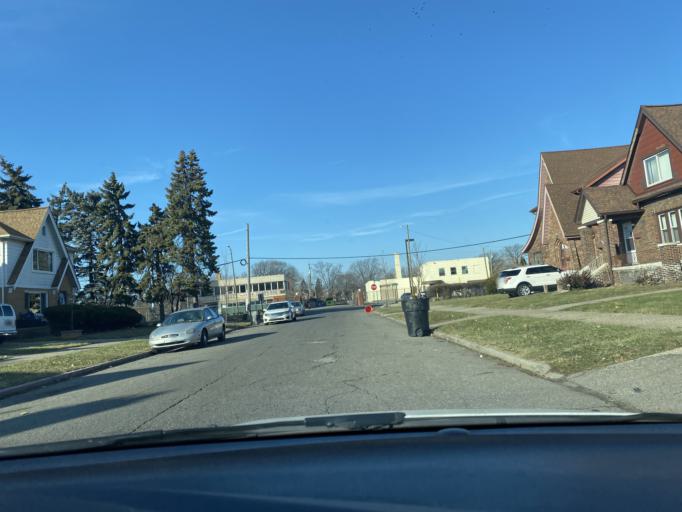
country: US
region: Michigan
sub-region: Wayne County
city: Harper Woods
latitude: 42.4091
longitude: -82.9456
